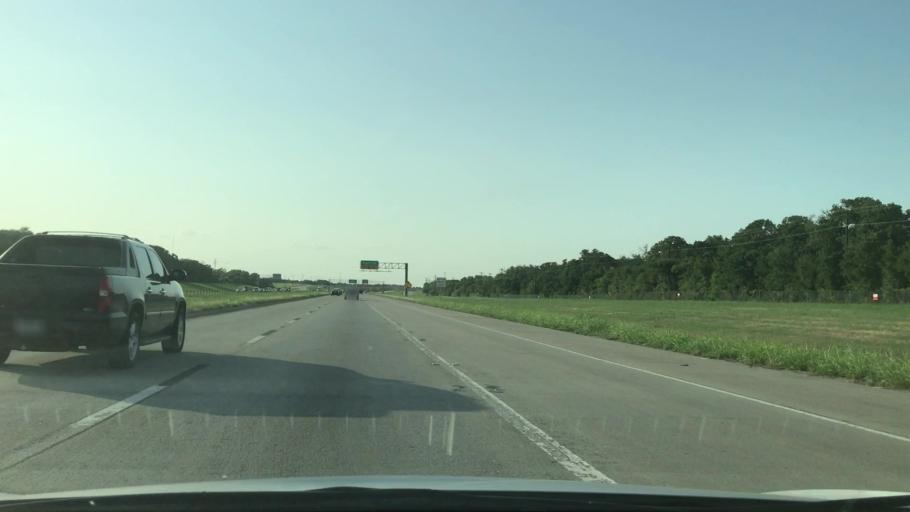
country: US
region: Texas
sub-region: Tarrant County
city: Euless
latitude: 32.8727
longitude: -97.0690
